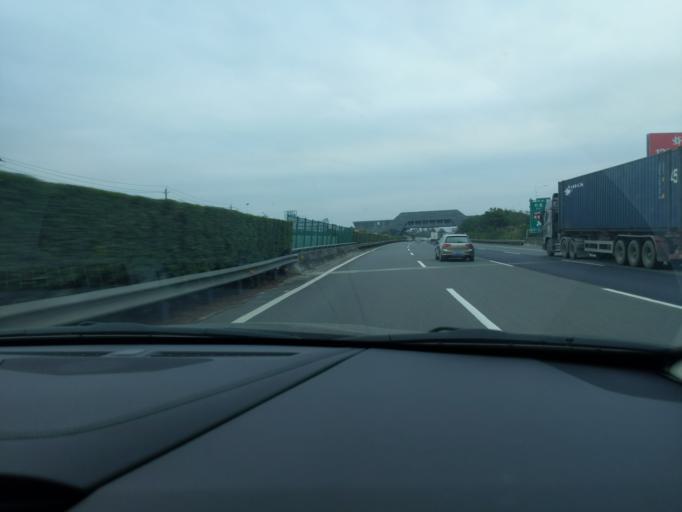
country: CN
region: Fujian
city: Anhai
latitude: 24.7457
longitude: 118.4298
